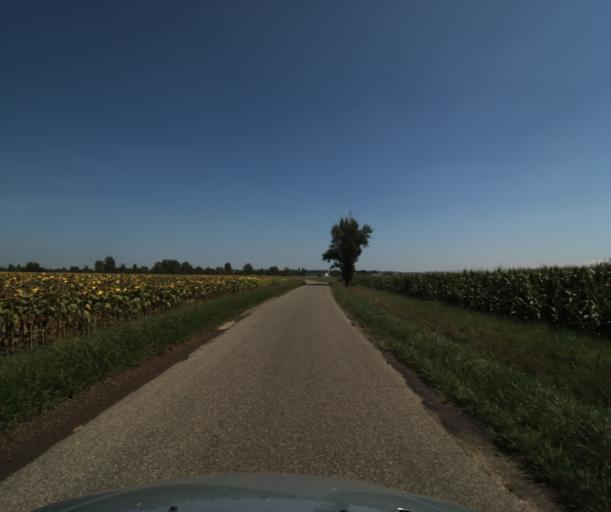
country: FR
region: Midi-Pyrenees
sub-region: Departement de la Haute-Garonne
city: Labastidette
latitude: 43.4546
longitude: 1.2621
